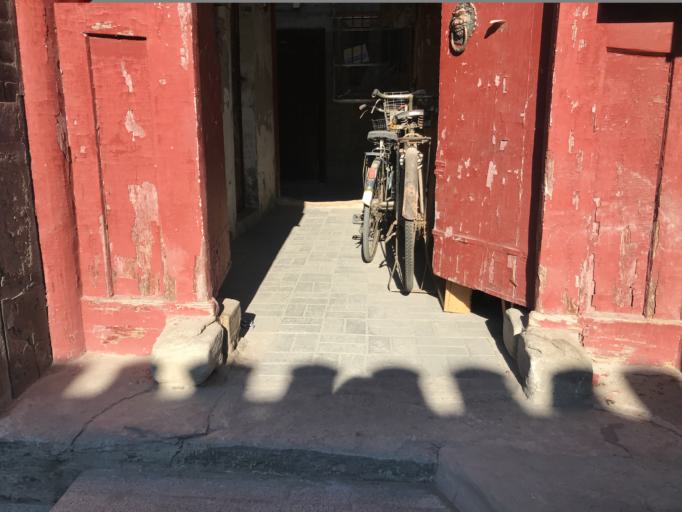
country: CN
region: Beijing
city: Beijing
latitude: 39.8917
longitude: 116.3908
